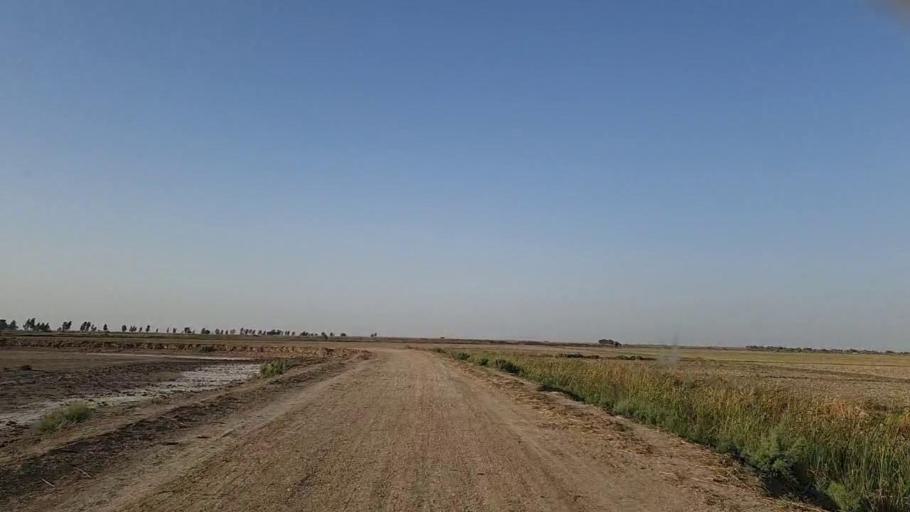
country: PK
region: Sindh
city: Jati
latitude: 24.4207
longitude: 68.2947
